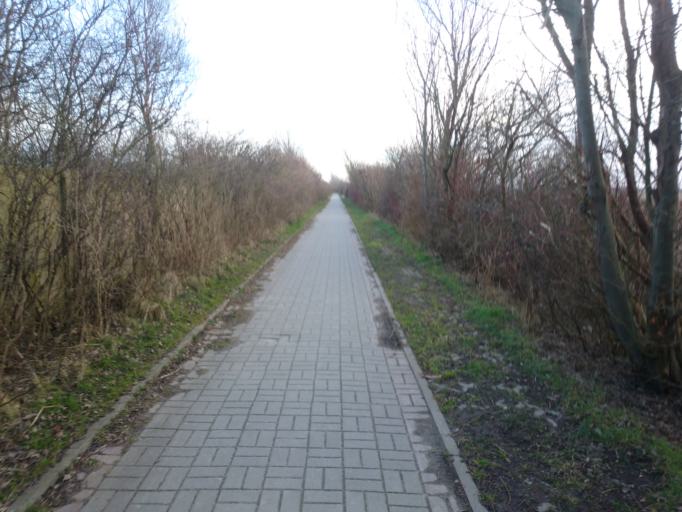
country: DE
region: Mecklenburg-Vorpommern
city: Elmenhorst
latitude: 54.1702
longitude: 11.9816
